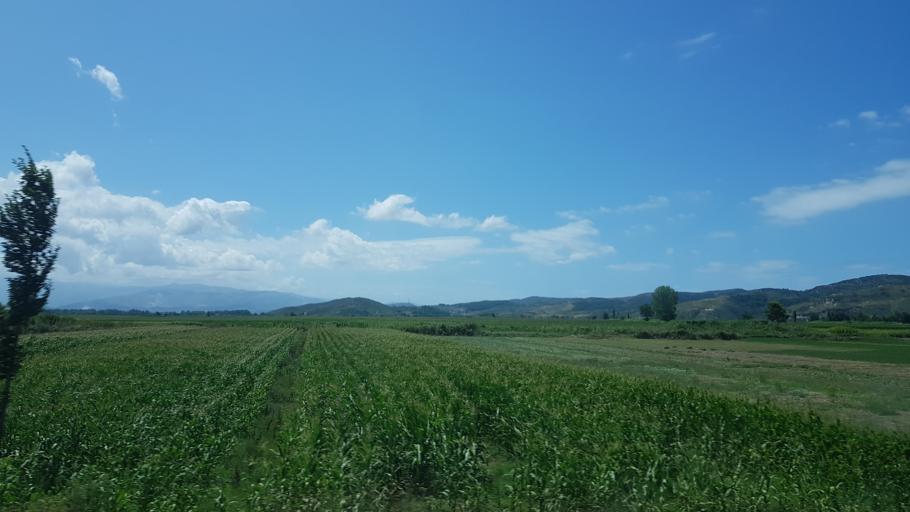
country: AL
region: Fier
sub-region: Rrethi i Fierit
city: Cakran
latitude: 40.6027
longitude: 19.5567
